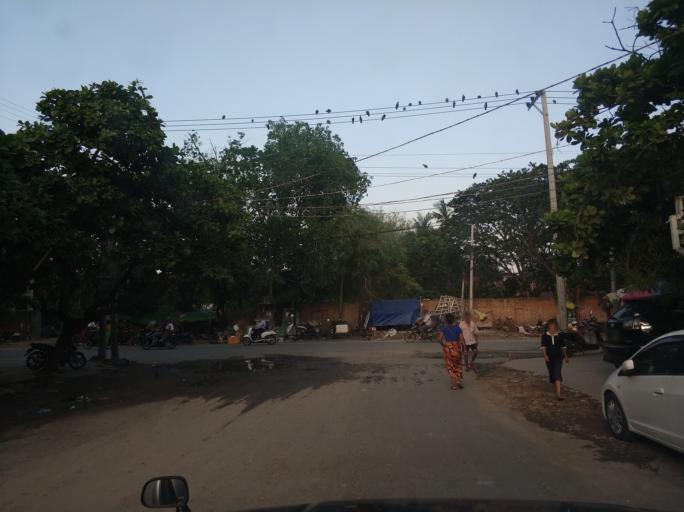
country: MM
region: Mandalay
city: Mandalay
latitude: 21.9801
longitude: 96.0852
